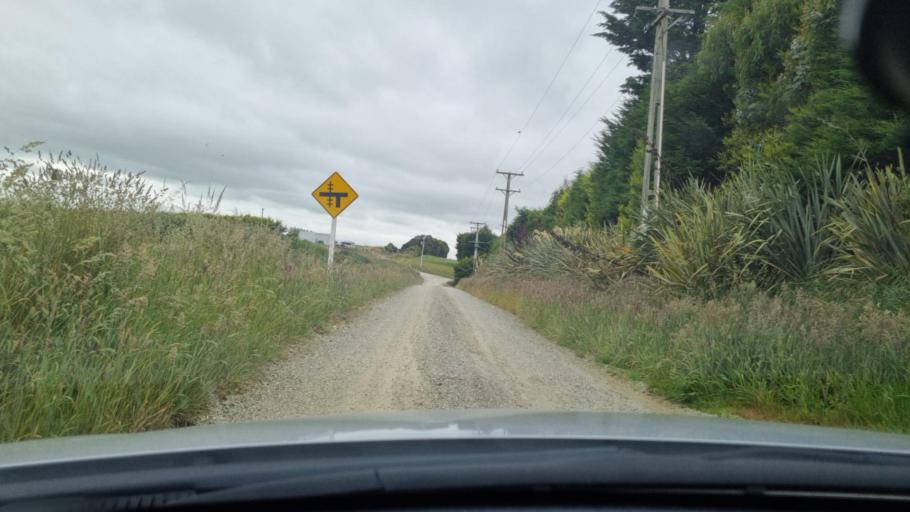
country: NZ
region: Southland
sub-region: Invercargill City
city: Invercargill
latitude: -46.3238
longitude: 168.3406
